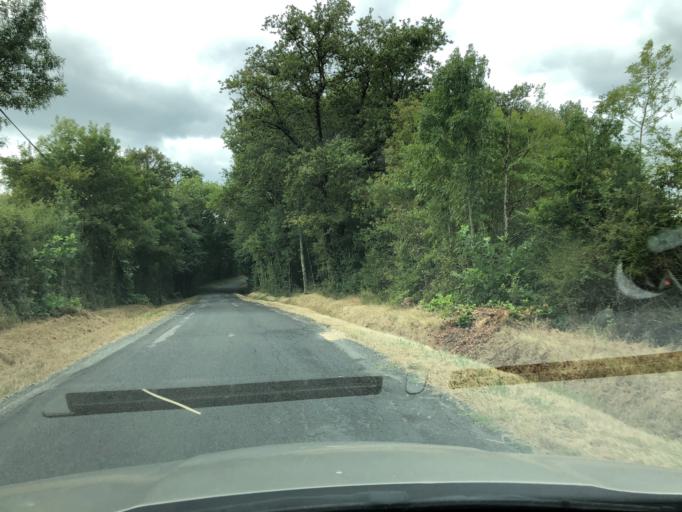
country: FR
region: Centre
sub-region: Departement d'Indre-et-Loire
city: Mazieres-de-Touraine
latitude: 47.3856
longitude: 0.4370
